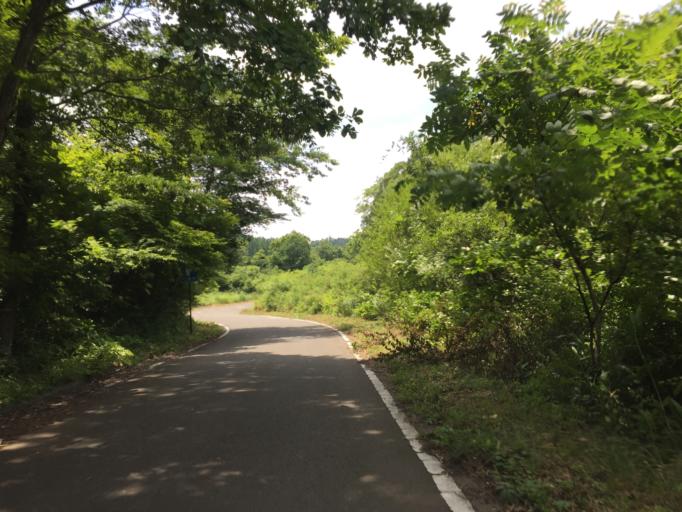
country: JP
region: Miyagi
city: Marumori
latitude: 37.7572
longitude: 140.7414
